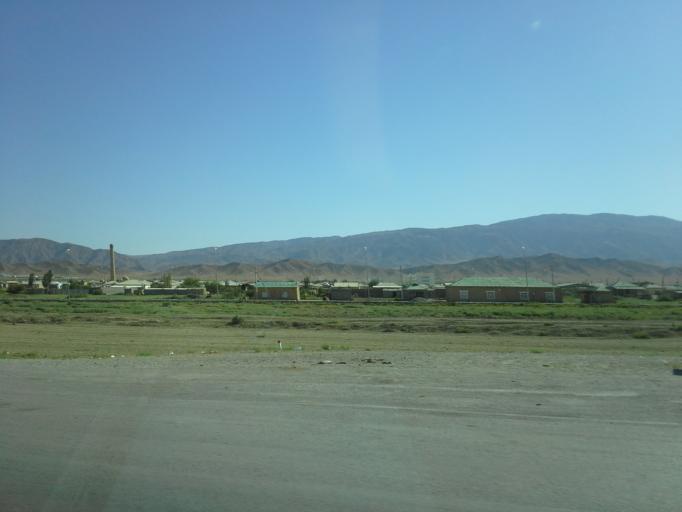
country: TM
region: Ahal
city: Baharly
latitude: 38.3798
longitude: 57.5027
